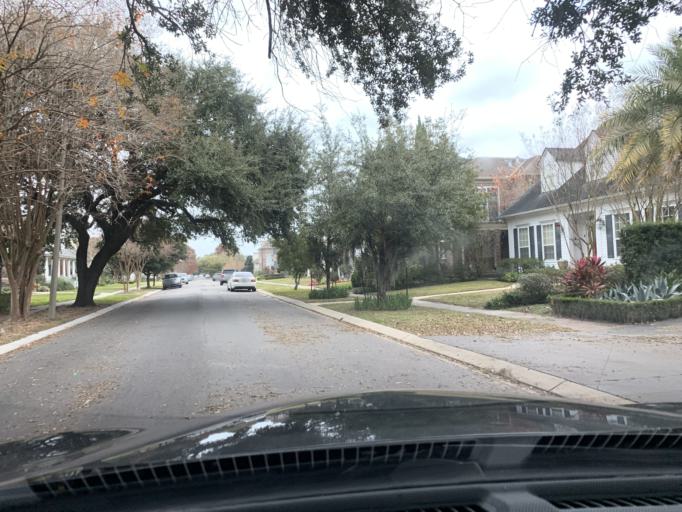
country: US
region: Louisiana
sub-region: Jefferson Parish
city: Metairie
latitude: 30.0044
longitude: -90.1015
